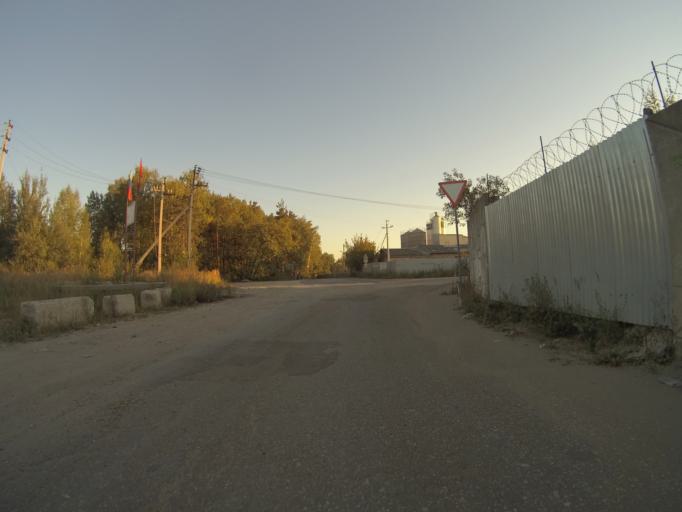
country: RU
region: Vladimir
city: Vladimir
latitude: 56.0930
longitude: 40.3703
